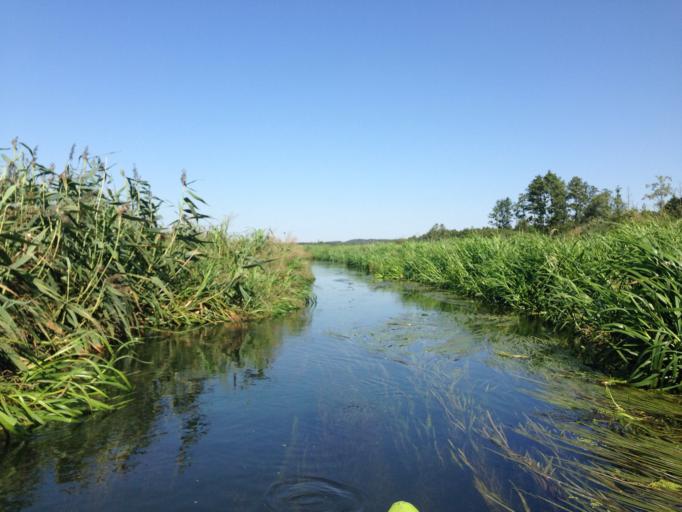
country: PL
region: Kujawsko-Pomorskie
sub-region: Powiat brodnicki
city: Bartniczka
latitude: 53.2624
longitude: 19.5990
